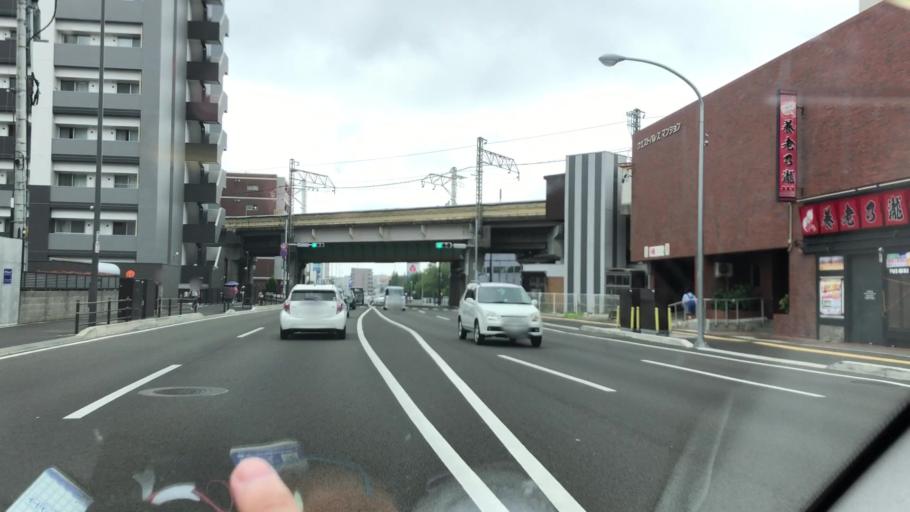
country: JP
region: Miyagi
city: Sendai-shi
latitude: 38.2689
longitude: 140.9182
